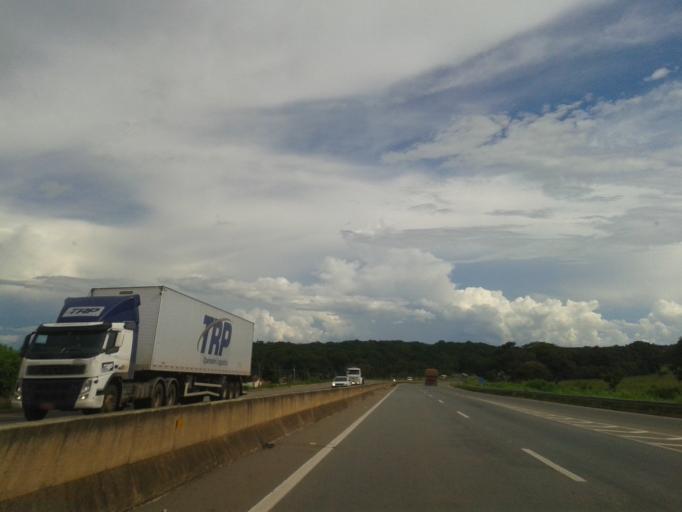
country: BR
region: Goias
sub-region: Hidrolandia
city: Hidrolandia
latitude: -16.9748
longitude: -49.2305
